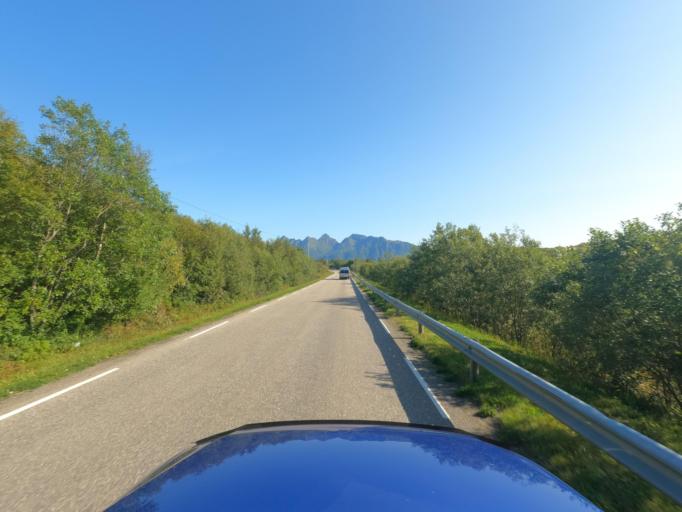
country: NO
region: Nordland
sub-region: Vagan
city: Svolvaer
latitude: 68.2443
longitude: 14.6493
